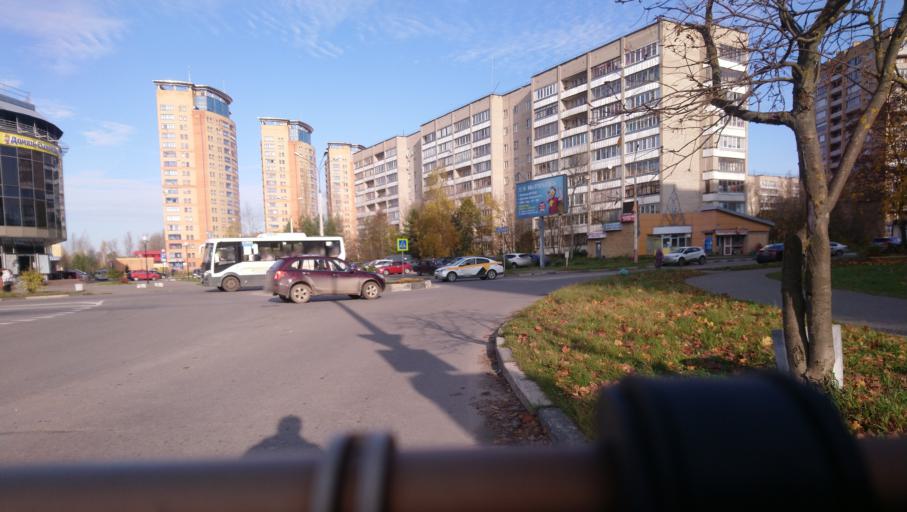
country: RU
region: Moskovskaya
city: Dubna
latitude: 56.7387
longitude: 37.1695
